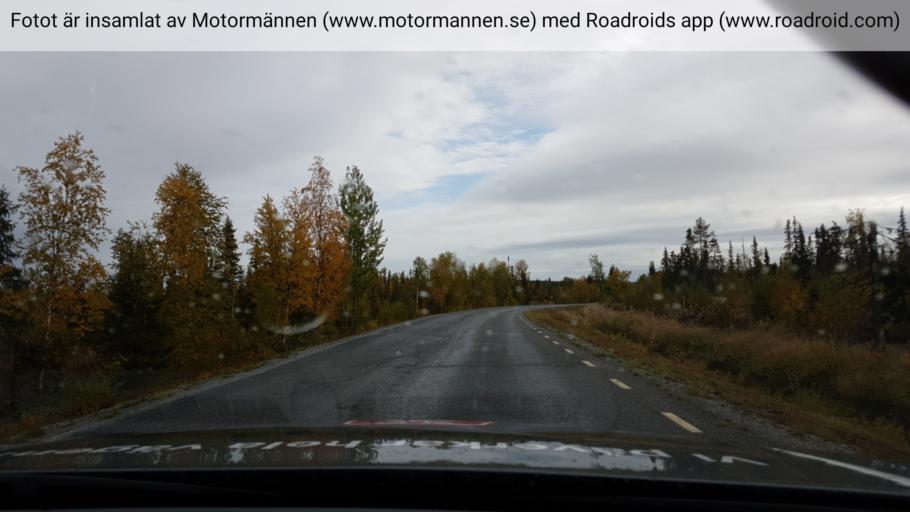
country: SE
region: Vaesterbotten
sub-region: Vilhelmina Kommun
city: Sjoberg
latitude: 64.7503
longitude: 16.1704
